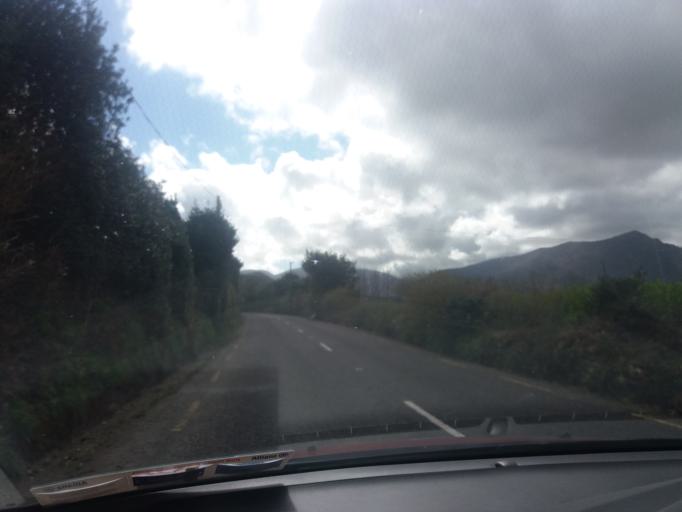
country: IE
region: Munster
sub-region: Ciarrai
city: Dingle
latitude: 52.2221
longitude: -10.1422
